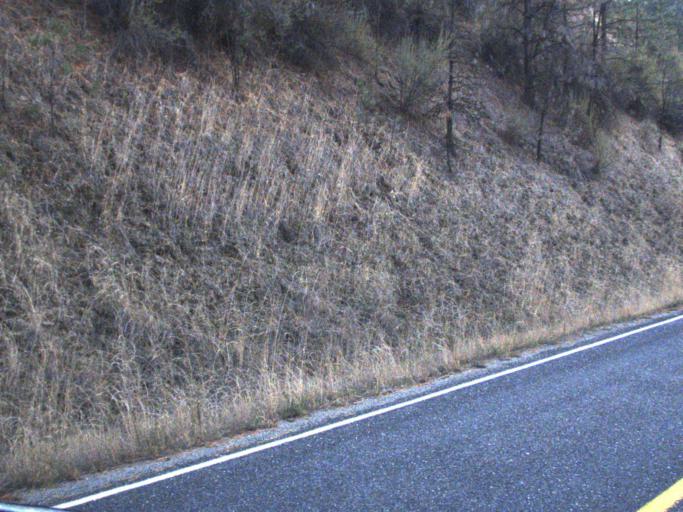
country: US
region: Washington
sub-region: Stevens County
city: Kettle Falls
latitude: 48.2296
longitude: -118.1563
